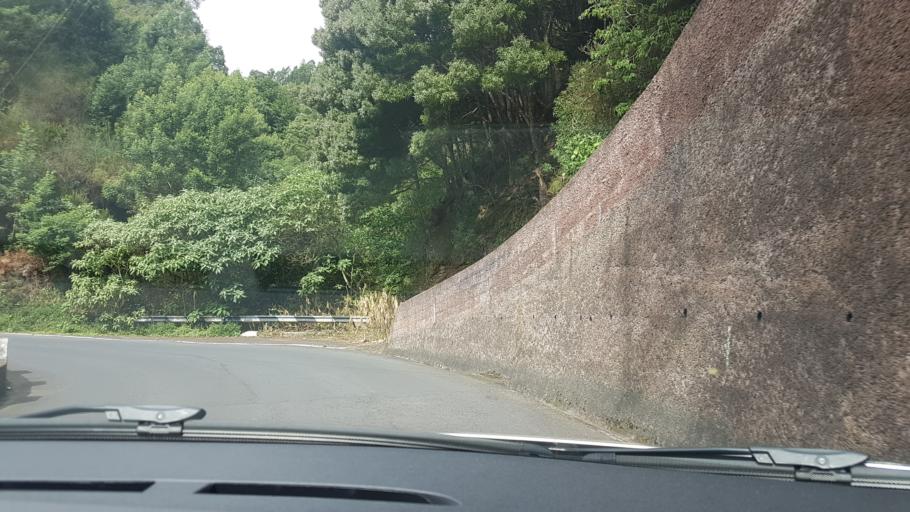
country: PT
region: Madeira
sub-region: Santa Cruz
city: Santa Cruz
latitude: 32.7366
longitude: -16.8120
